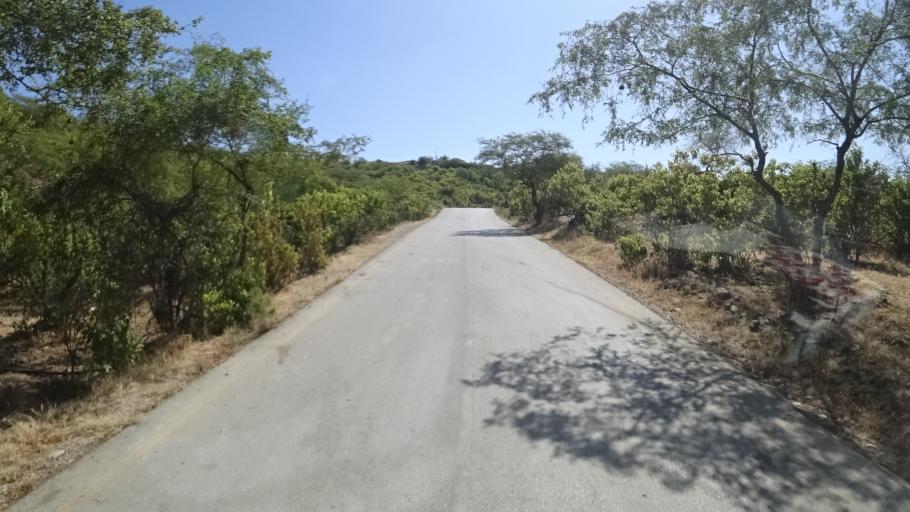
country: OM
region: Zufar
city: Salalah
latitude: 17.0717
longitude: 54.4452
